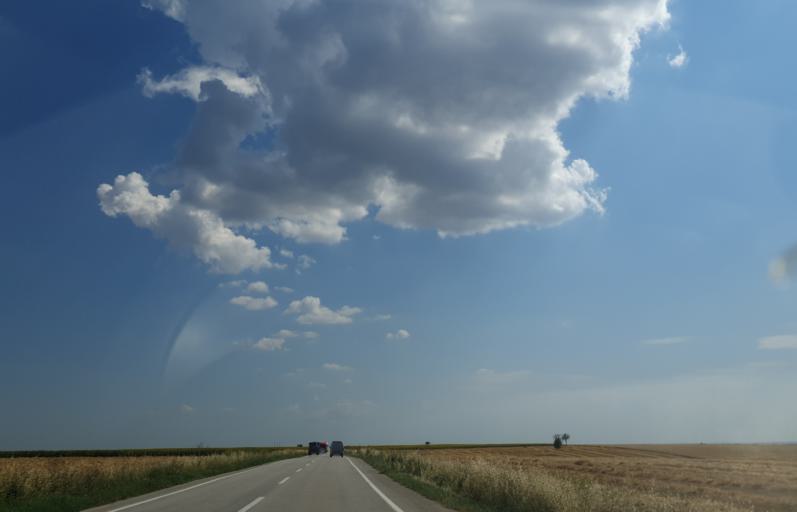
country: TR
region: Kirklareli
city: Buyukkaristiran
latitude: 41.4105
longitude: 27.5771
